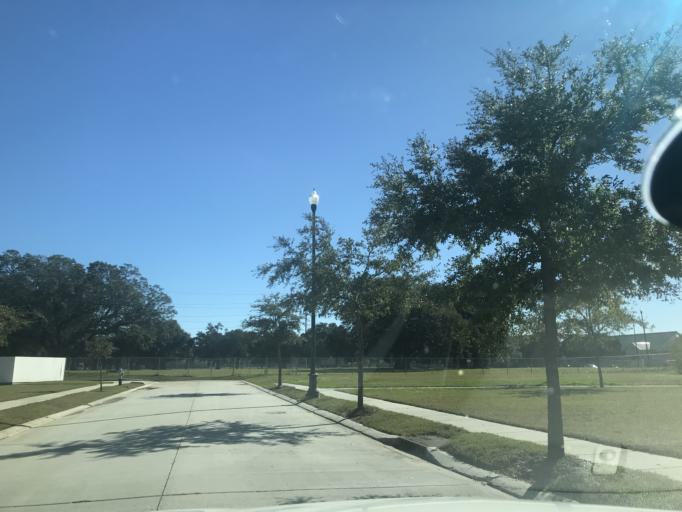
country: US
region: Louisiana
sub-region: Orleans Parish
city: New Orleans
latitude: 29.9523
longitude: -90.0933
